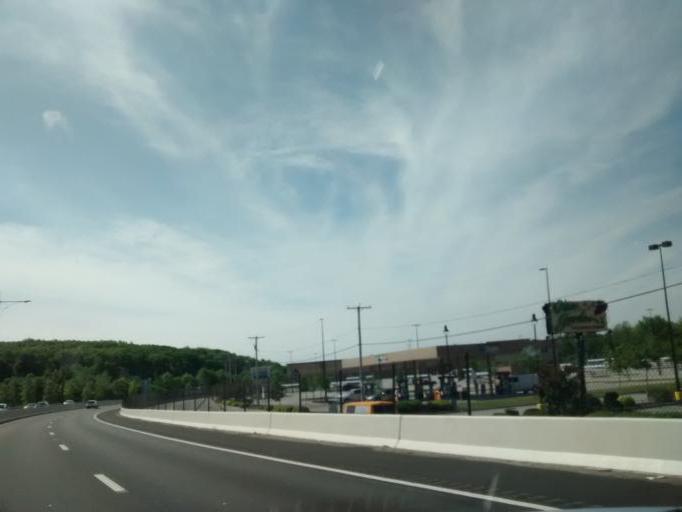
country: US
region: Massachusetts
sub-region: Worcester County
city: Sunderland
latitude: 42.2325
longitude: -71.7881
